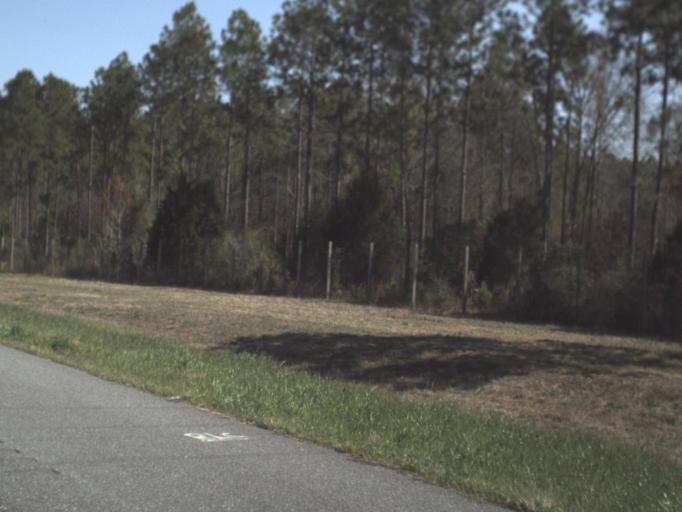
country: US
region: Florida
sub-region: Washington County
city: Chipley
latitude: 30.7476
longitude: -85.4134
